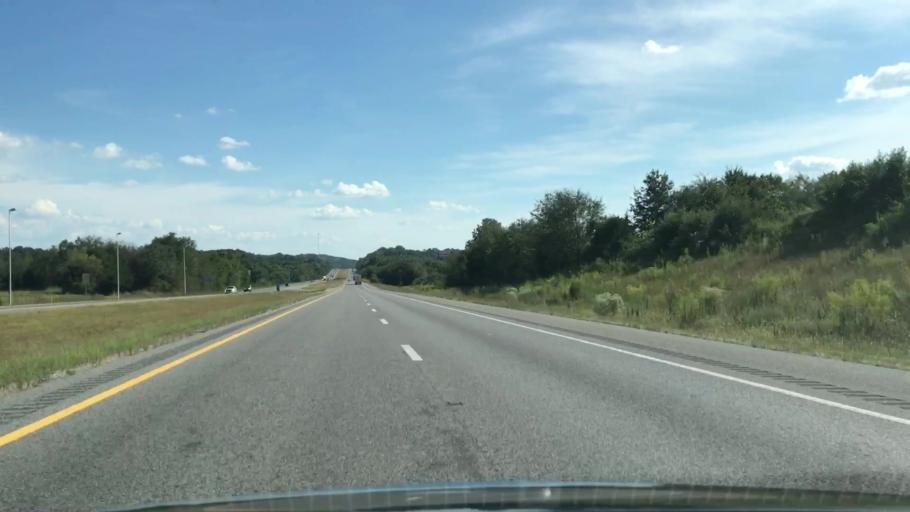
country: US
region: Alabama
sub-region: Limestone County
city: Ardmore
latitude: 35.0582
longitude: -86.8814
